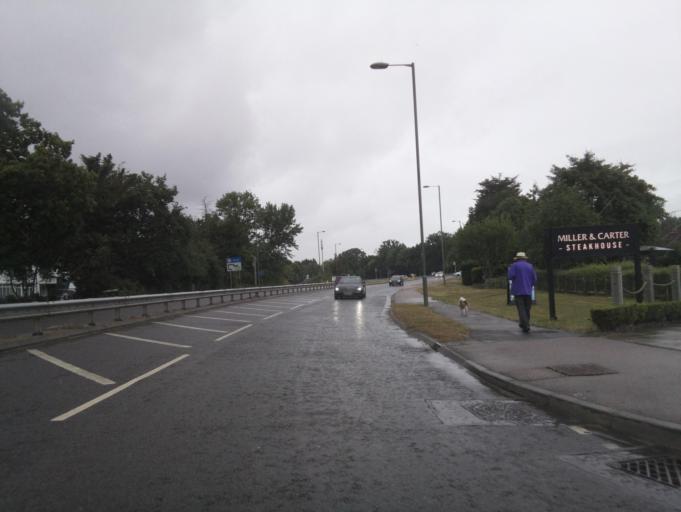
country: GB
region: England
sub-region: Surrey
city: Salfords
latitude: 51.2024
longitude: -0.1668
